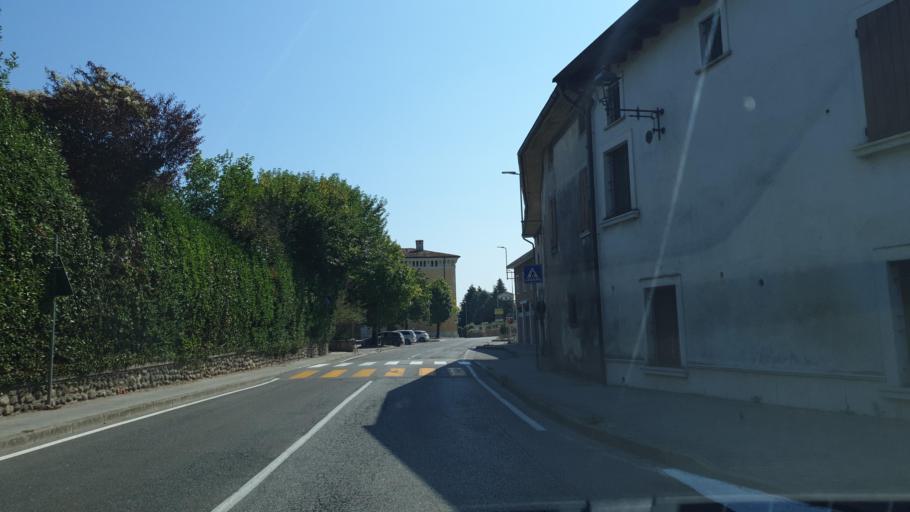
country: IT
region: Lombardy
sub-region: Provincia di Brescia
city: Carzago Riviera
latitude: 45.5272
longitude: 10.4527
